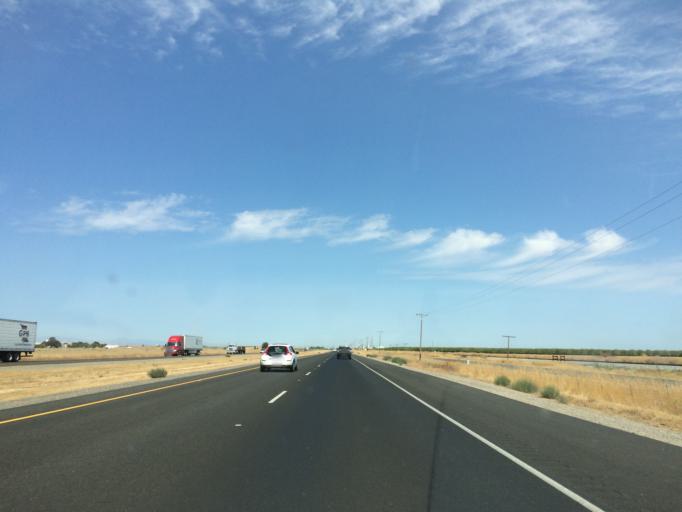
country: US
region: California
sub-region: Yolo County
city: Dunnigan
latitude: 38.9417
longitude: -122.0074
